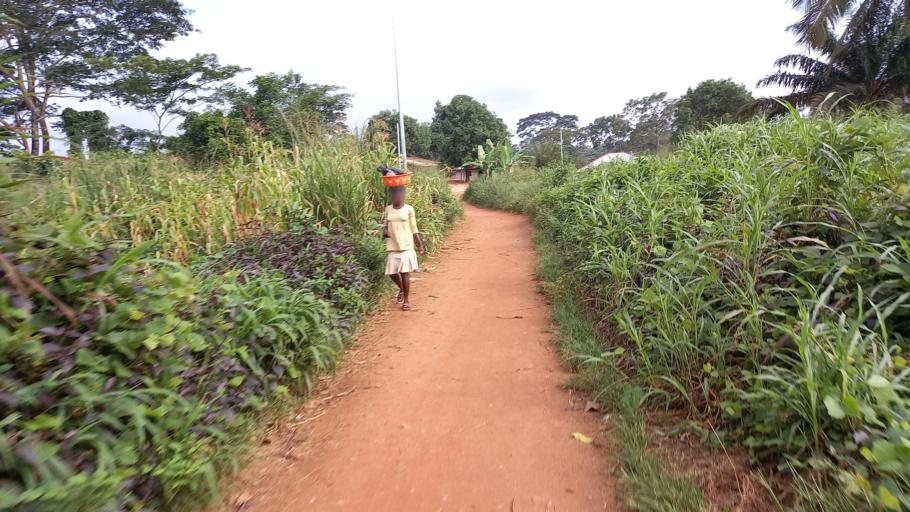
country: SL
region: Eastern Province
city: Kailahun
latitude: 8.2778
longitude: -10.5781
